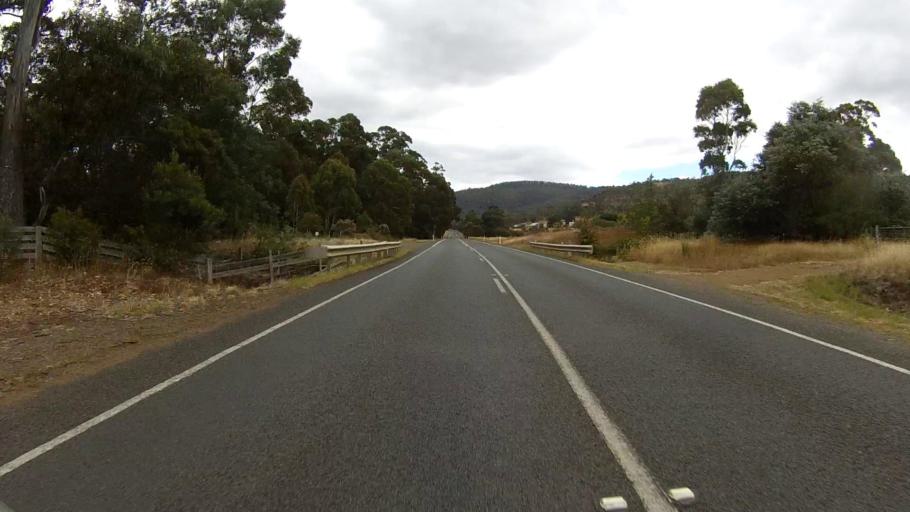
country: AU
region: Tasmania
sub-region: Sorell
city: Sorell
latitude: -42.6994
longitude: 147.5249
